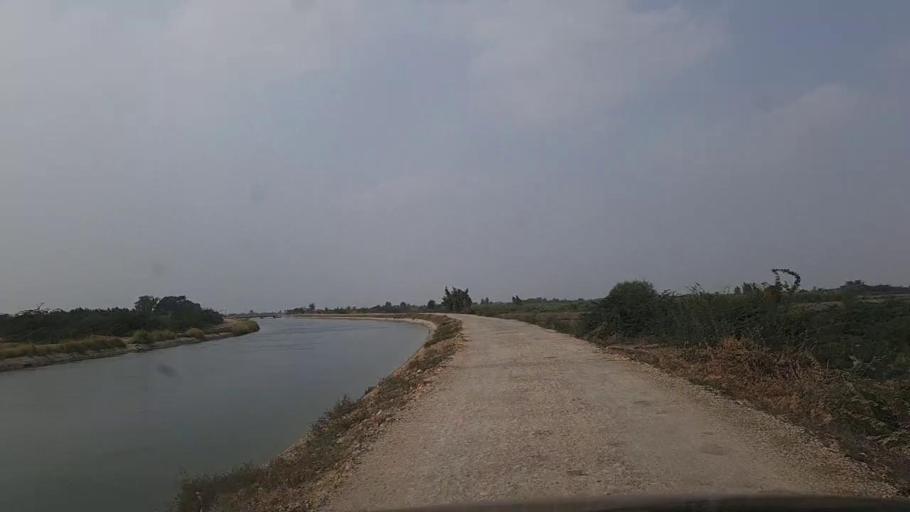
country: PK
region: Sindh
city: Thatta
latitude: 24.8024
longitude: 67.9049
